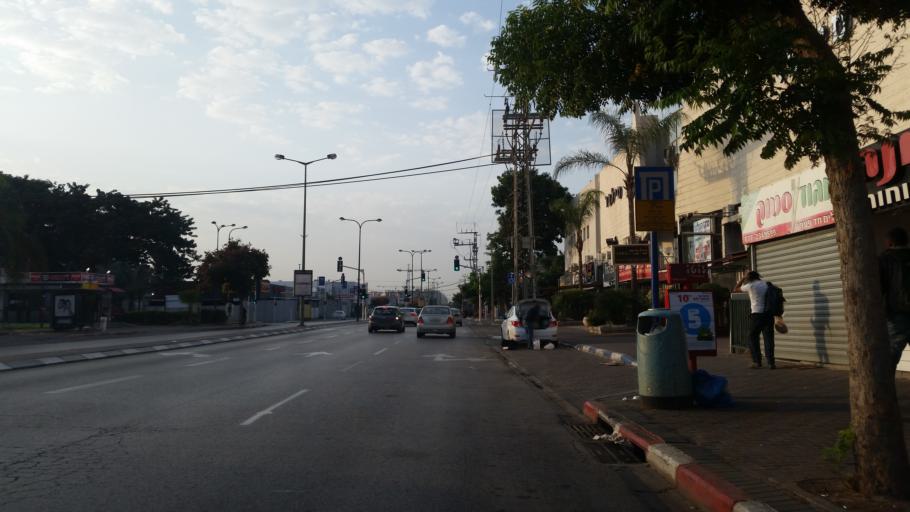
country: IL
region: Central District
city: Bet Yizhaq
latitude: 32.3211
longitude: 34.8743
